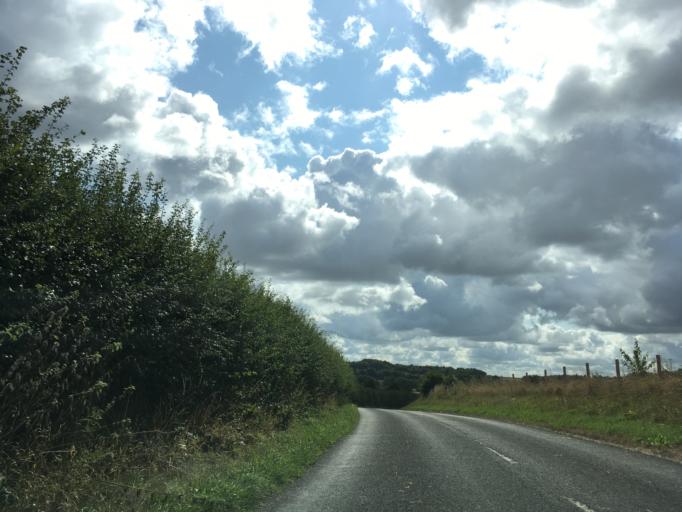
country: GB
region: England
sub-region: Hampshire
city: Overton
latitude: 51.2084
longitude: -1.3716
